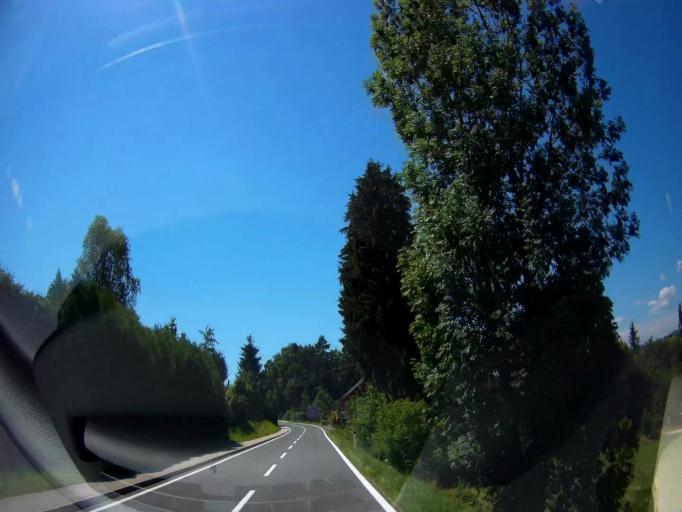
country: AT
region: Carinthia
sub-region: Politischer Bezirk Volkermarkt
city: Eberndorf
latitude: 46.6132
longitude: 14.5796
